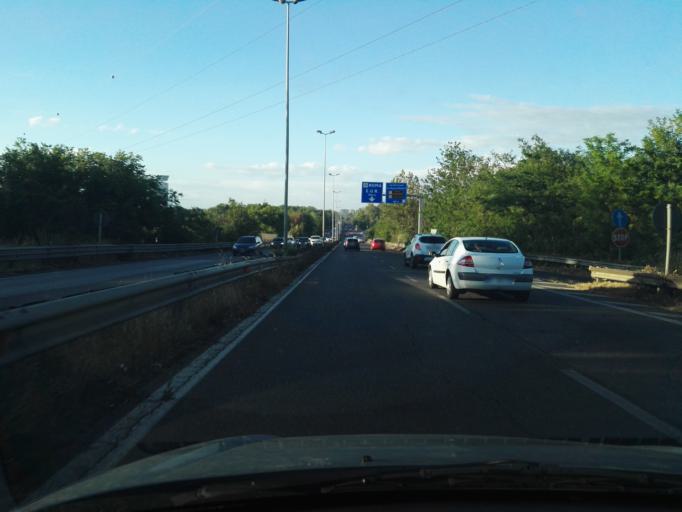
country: IT
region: Latium
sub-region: Citta metropolitana di Roma Capitale
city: Selcetta
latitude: 41.8062
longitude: 12.4559
